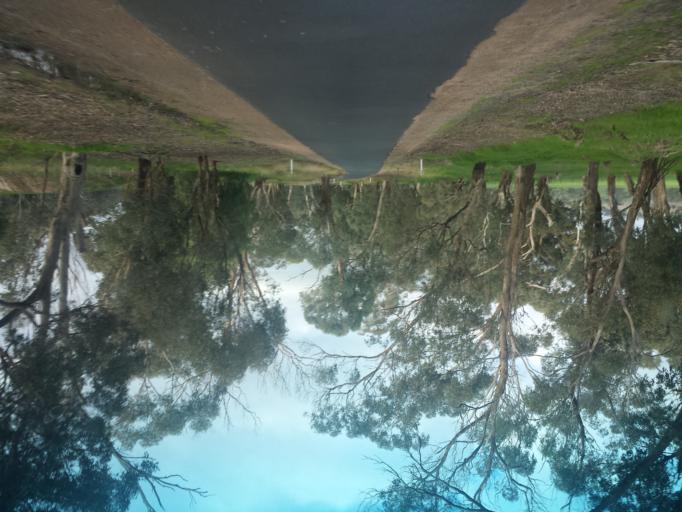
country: AU
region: Victoria
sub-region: Murrindindi
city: Kinglake West
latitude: -36.9189
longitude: 145.2256
